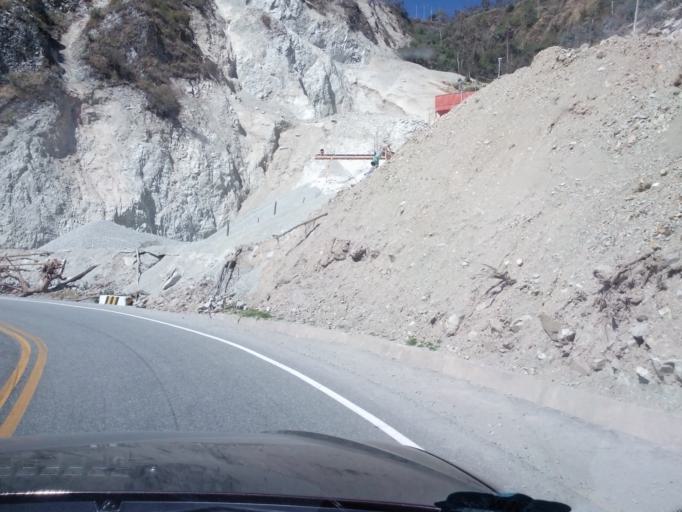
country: PE
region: Cusco
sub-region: Provincia de Anta
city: Ancahuasi
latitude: -13.4475
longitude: -72.3746
